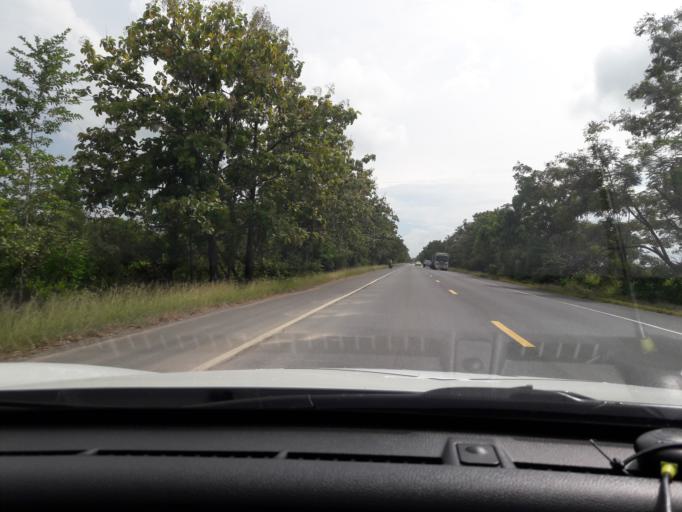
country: TH
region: Nakhon Sawan
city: Phai Sali
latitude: 15.5697
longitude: 100.5590
